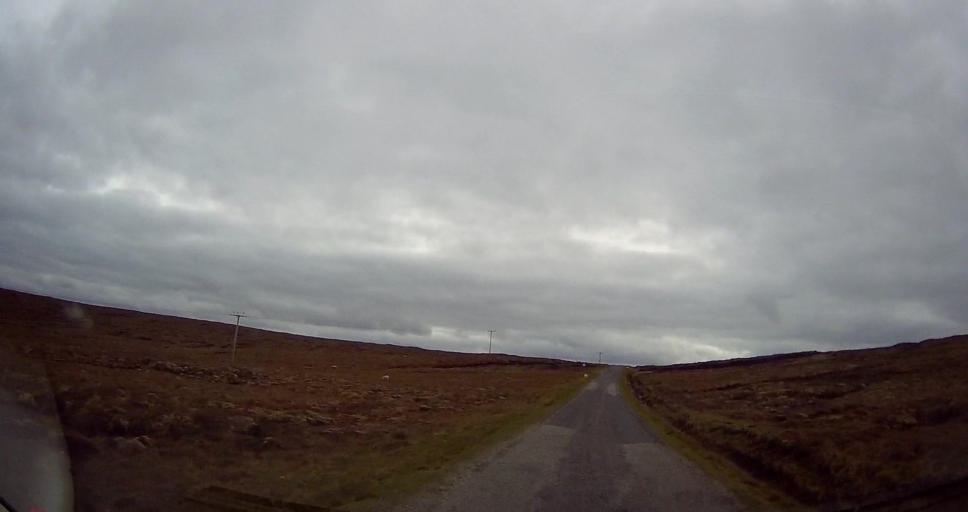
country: GB
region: Scotland
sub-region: Shetland Islands
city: Shetland
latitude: 60.5099
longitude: -1.1291
